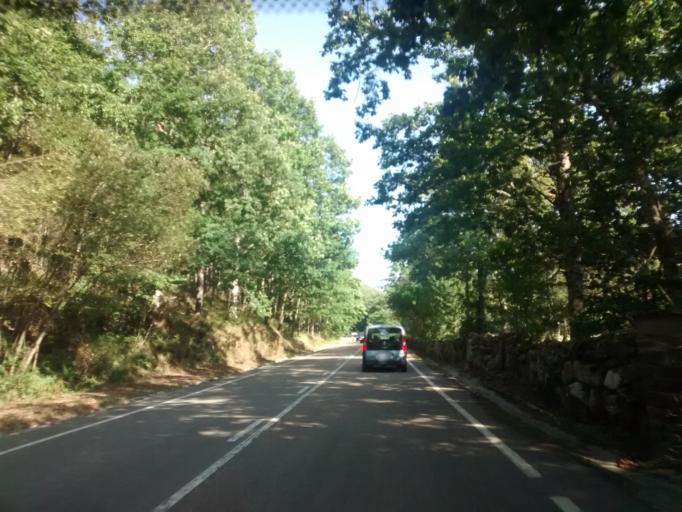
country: ES
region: Cantabria
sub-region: Provincia de Cantabria
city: Ruente
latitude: 43.1521
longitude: -4.2227
